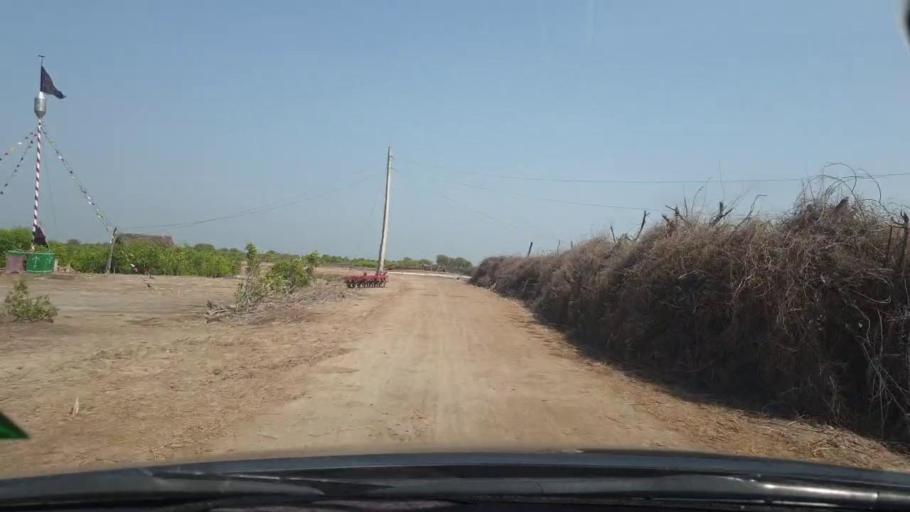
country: PK
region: Sindh
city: Tando Bago
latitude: 24.8027
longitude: 69.1083
